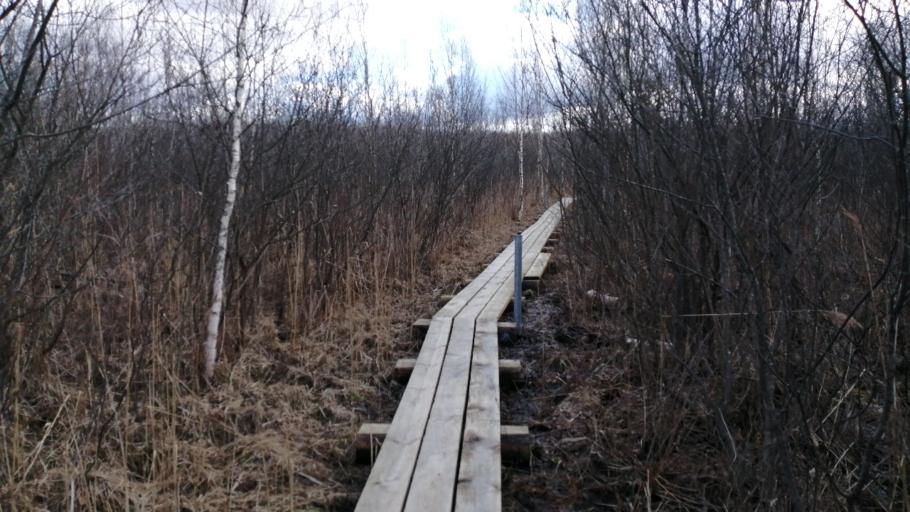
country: EE
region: Tartu
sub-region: Alatskivi vald
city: Kallaste
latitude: 58.3857
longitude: 27.1213
